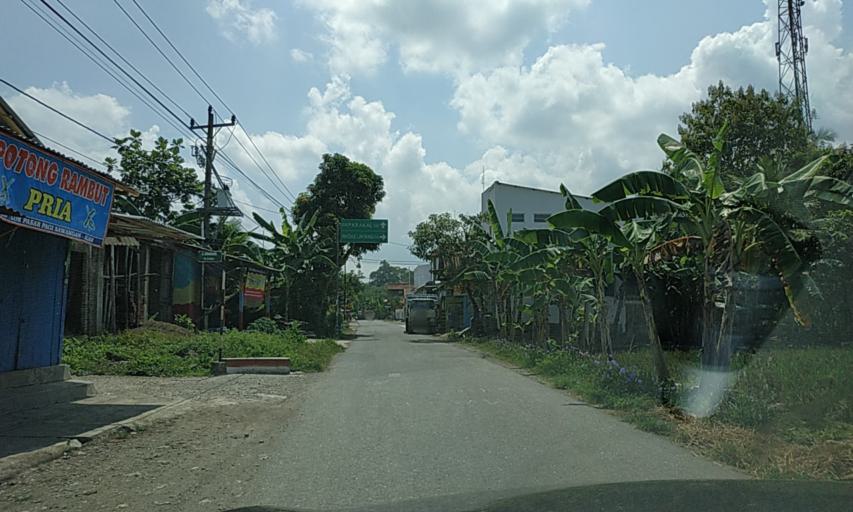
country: ID
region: Central Java
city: Gombong
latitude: -7.6343
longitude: 109.7073
